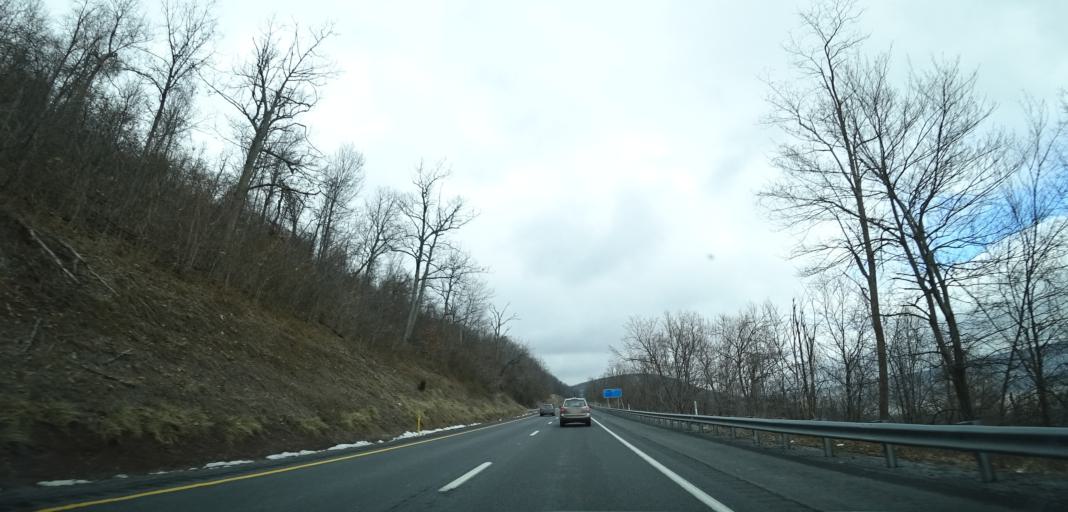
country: US
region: Pennsylvania
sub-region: Bedford County
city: Earlston
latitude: 39.8745
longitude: -78.2501
